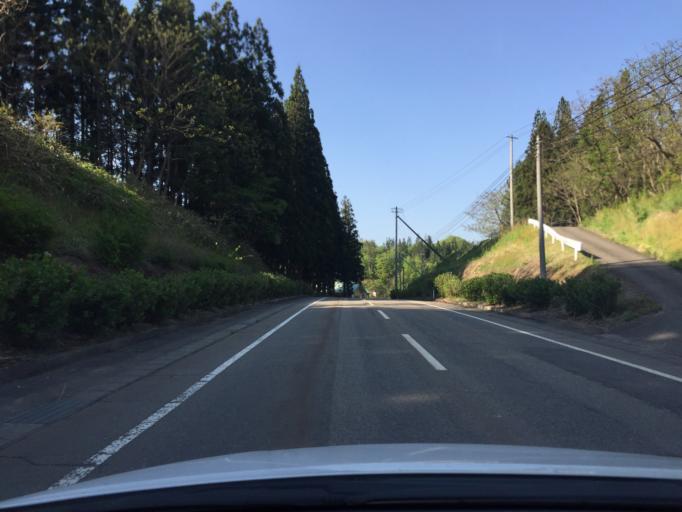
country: JP
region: Fukushima
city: Kitakata
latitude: 37.6771
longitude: 139.7912
